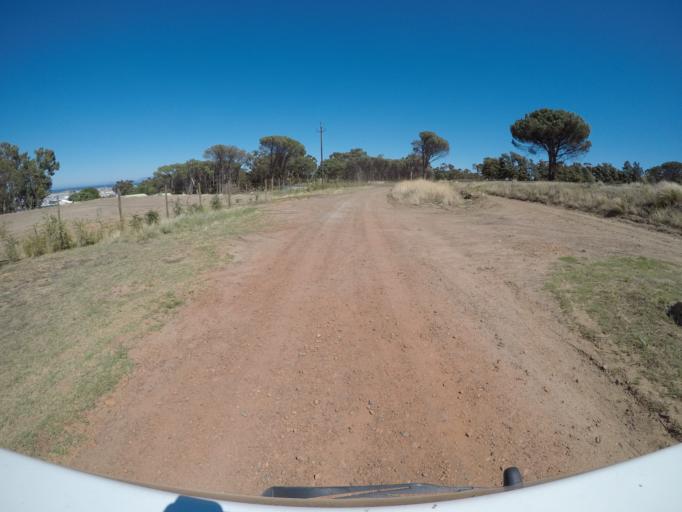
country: ZA
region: Western Cape
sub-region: Overberg District Municipality
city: Grabouw
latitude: -34.1154
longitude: 18.8808
